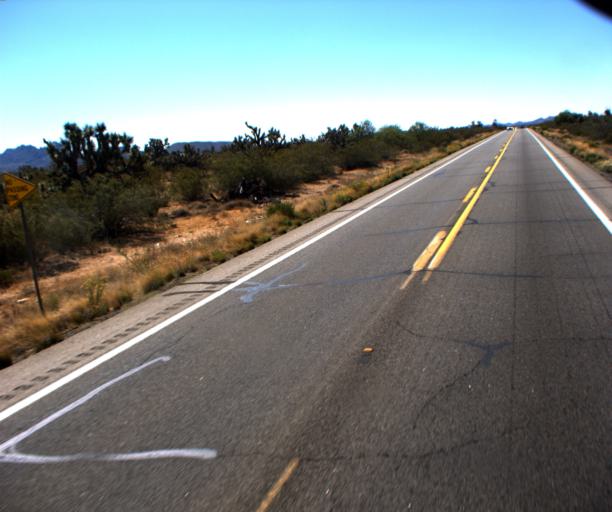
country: US
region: Arizona
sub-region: Yavapai County
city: Congress
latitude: 34.2414
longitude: -113.0766
